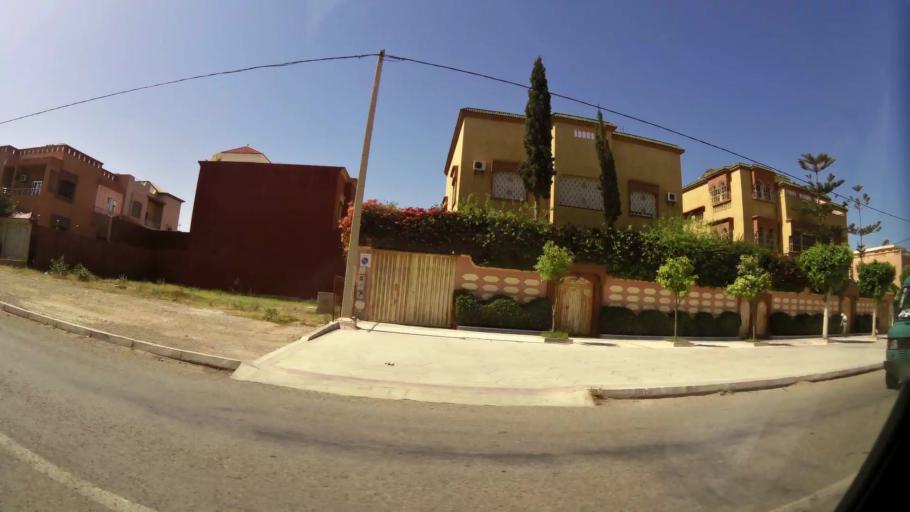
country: MA
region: Souss-Massa-Draa
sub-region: Inezgane-Ait Mellou
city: Inezgane
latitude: 30.3260
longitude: -9.5046
